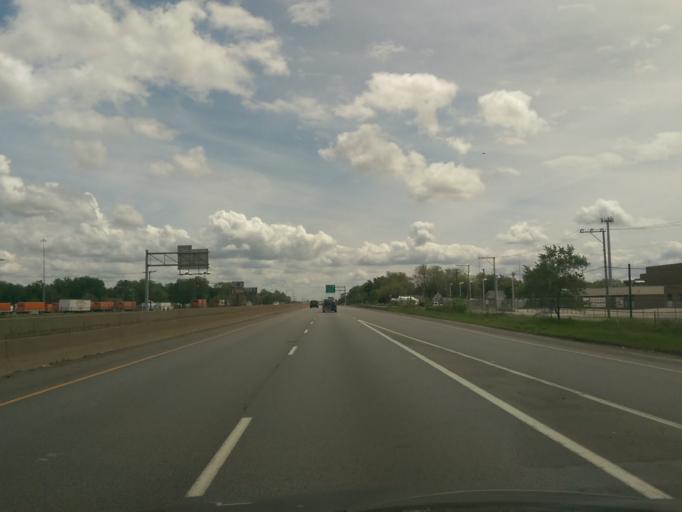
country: US
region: Indiana
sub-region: Lake County
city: Highland
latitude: 41.5865
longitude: -87.4329
